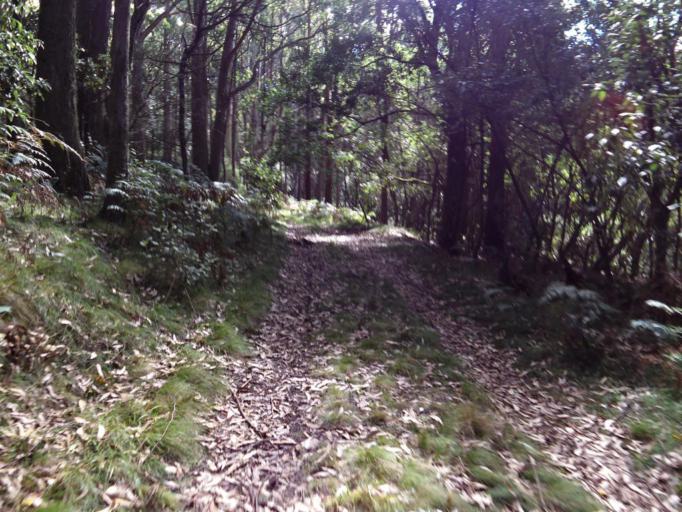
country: AU
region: Victoria
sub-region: Hume
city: Sunbury
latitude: -37.3730
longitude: 144.6133
